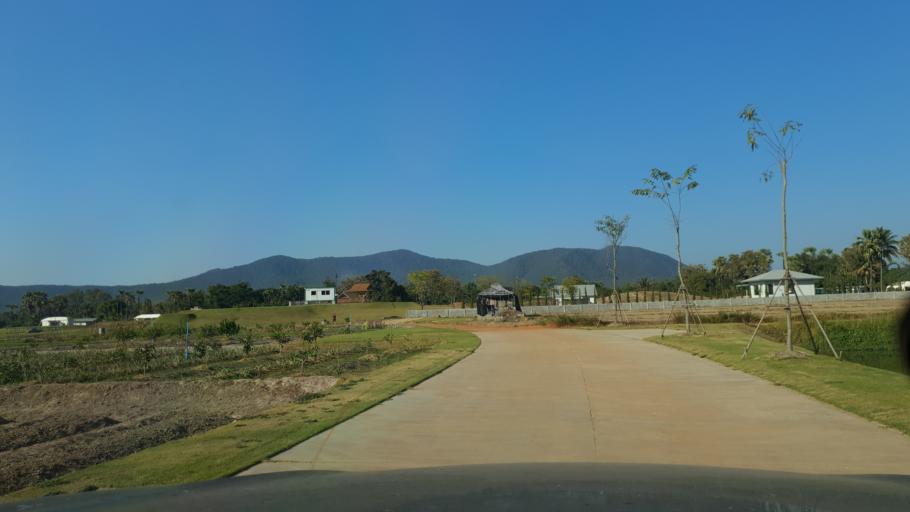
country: TH
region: Chiang Mai
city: Mae On
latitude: 18.7237
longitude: 99.2156
